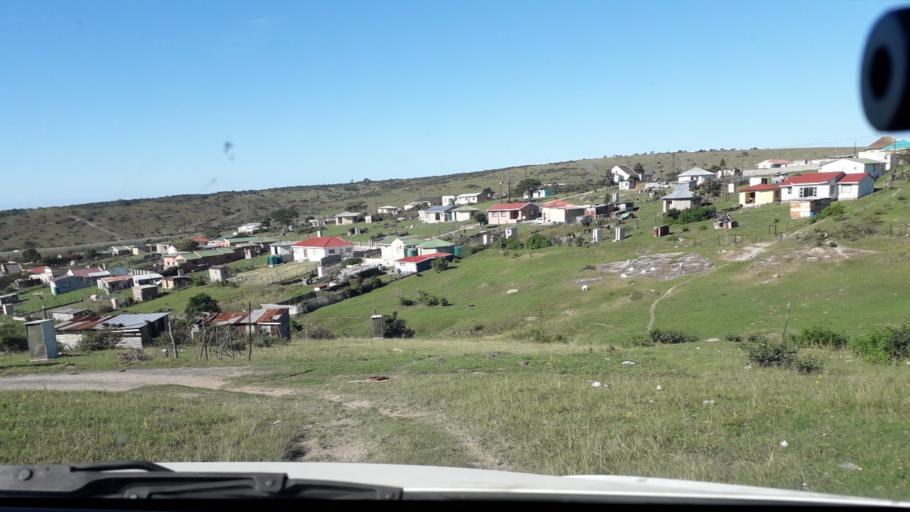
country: ZA
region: Eastern Cape
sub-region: Buffalo City Metropolitan Municipality
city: East London
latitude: -32.8437
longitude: 27.9910
